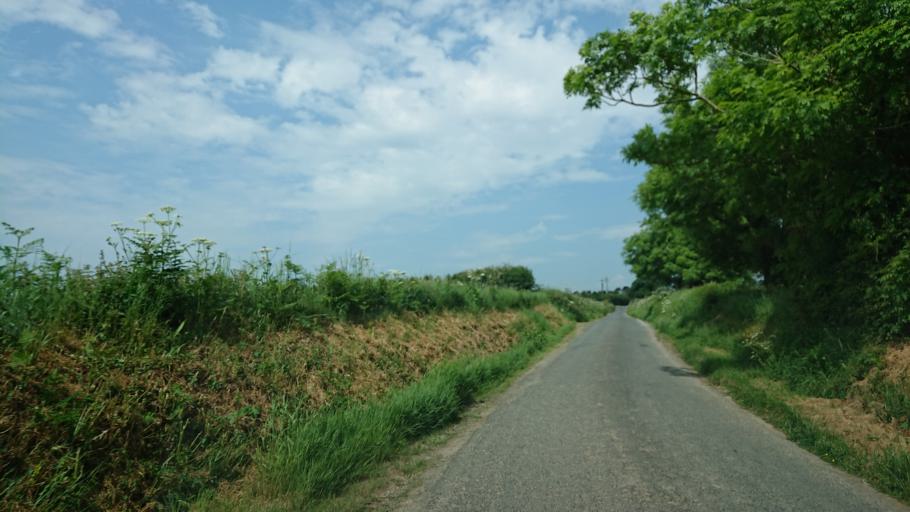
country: IE
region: Munster
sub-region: Waterford
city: Dunmore East
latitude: 52.2050
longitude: -6.9838
